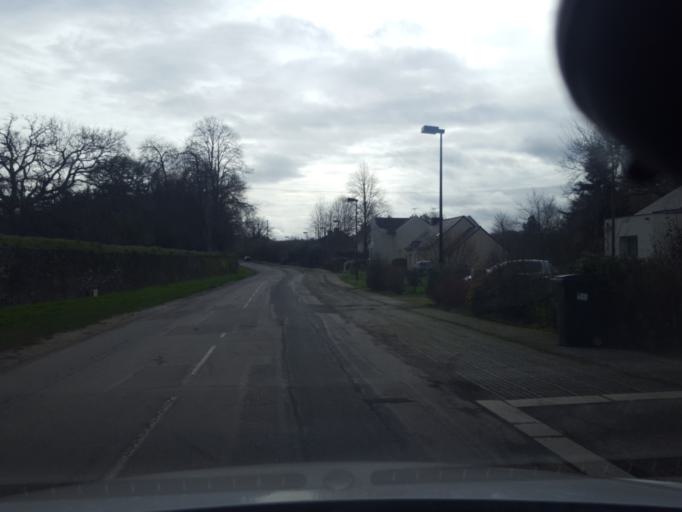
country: FR
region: Brittany
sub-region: Departement d'Ille-et-Vilaine
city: Guignen
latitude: 47.9179
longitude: -1.8609
